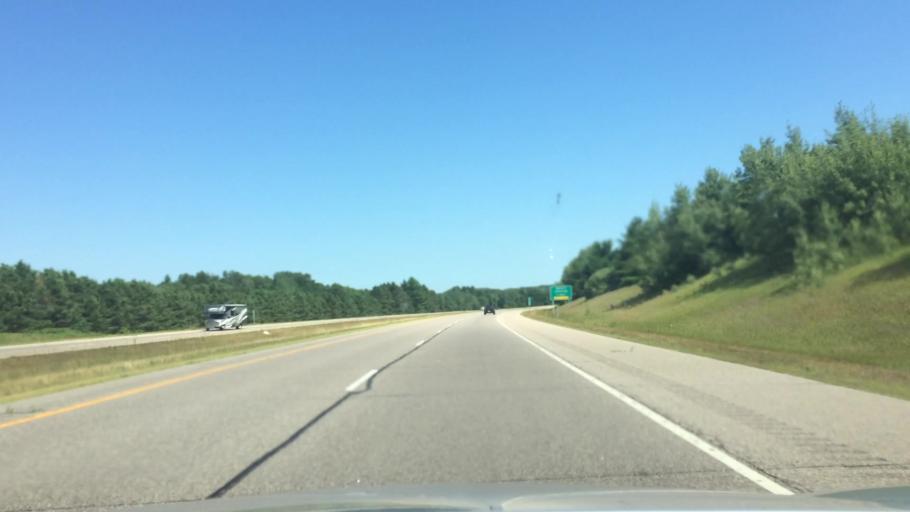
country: US
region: Wisconsin
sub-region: Marquette County
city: Westfield
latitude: 44.0584
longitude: -89.5421
